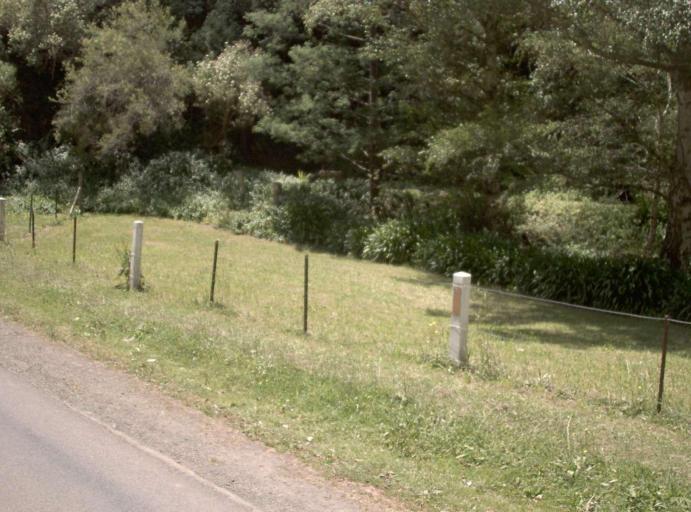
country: AU
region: Victoria
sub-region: Latrobe
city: Traralgon
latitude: -37.9452
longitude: 146.4504
